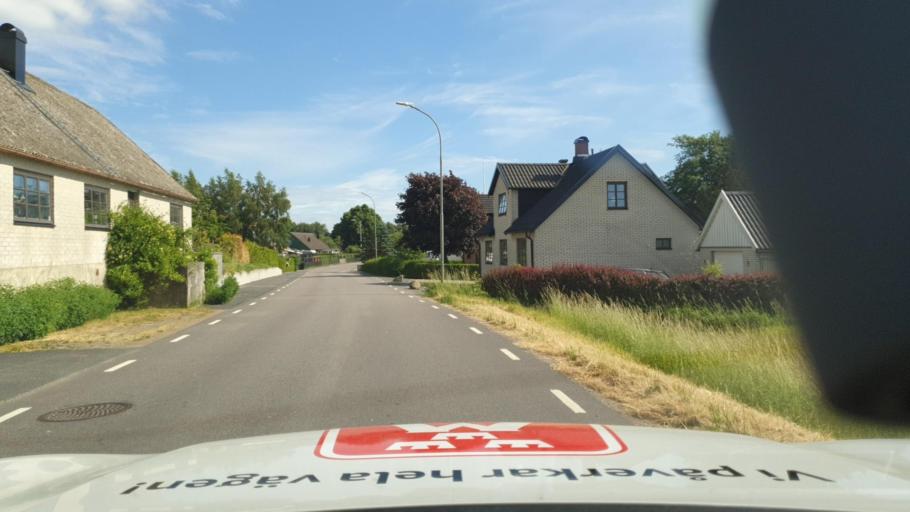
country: SE
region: Skane
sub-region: Skurups Kommun
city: Rydsgard
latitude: 55.5145
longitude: 13.5497
